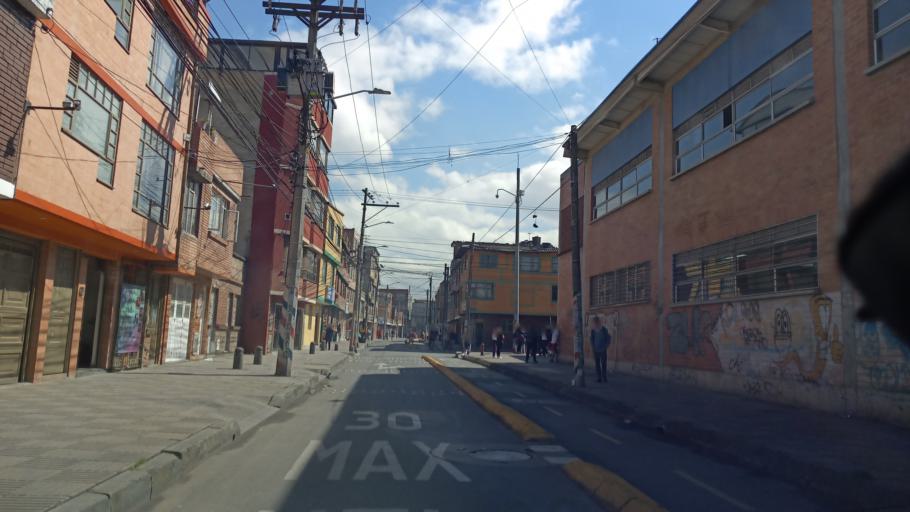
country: CO
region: Cundinamarca
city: Funza
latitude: 4.6726
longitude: -74.1493
